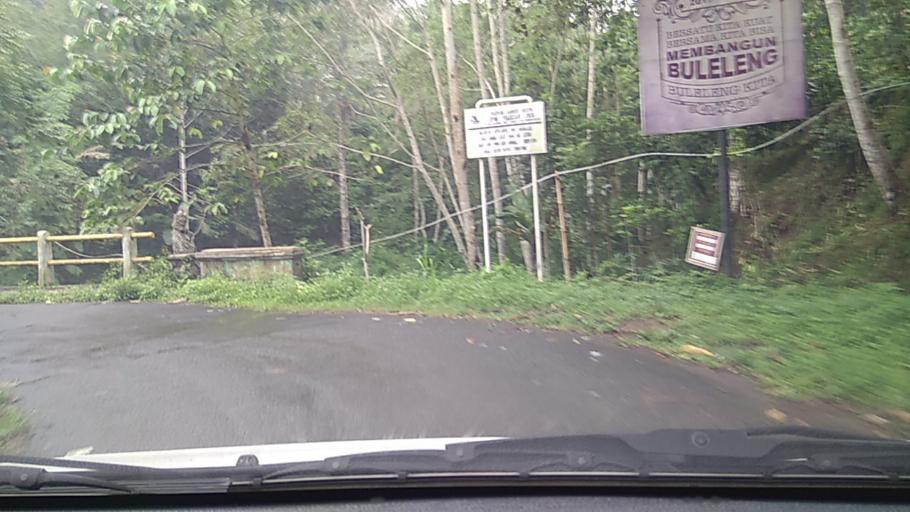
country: ID
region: Bali
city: Banjar Ambengan
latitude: -8.1980
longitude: 115.1786
